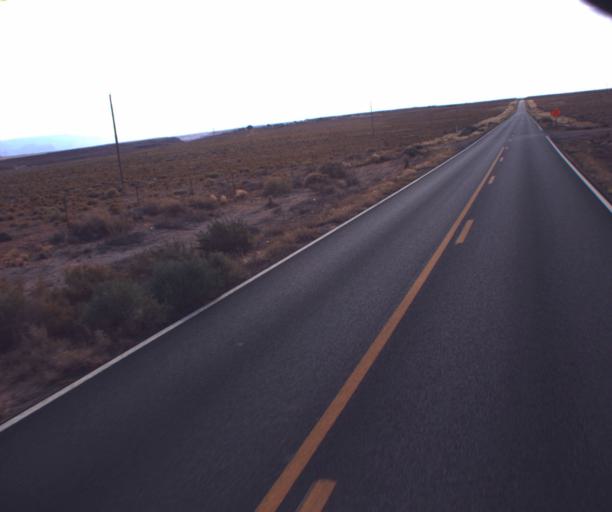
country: US
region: Arizona
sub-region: Apache County
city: Many Farms
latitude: 36.5964
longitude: -109.5664
